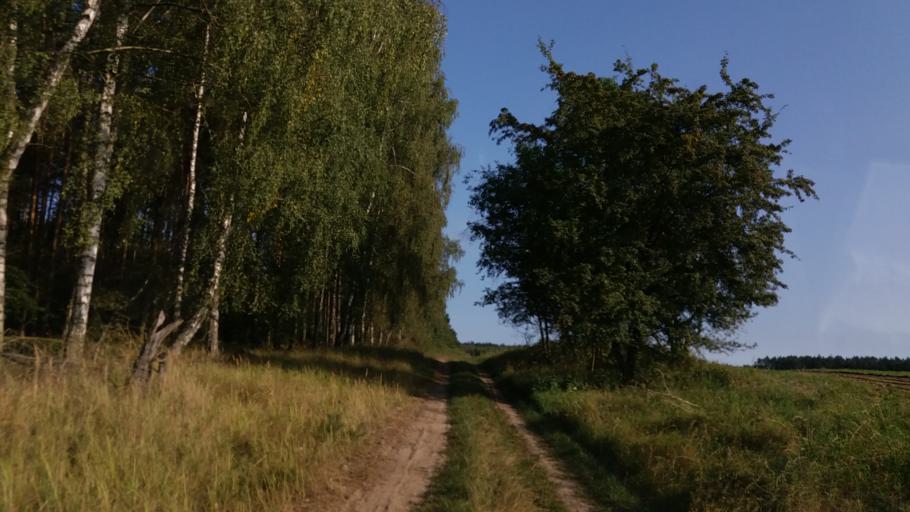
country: PL
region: West Pomeranian Voivodeship
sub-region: Powiat choszczenski
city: Recz
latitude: 53.1876
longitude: 15.5412
